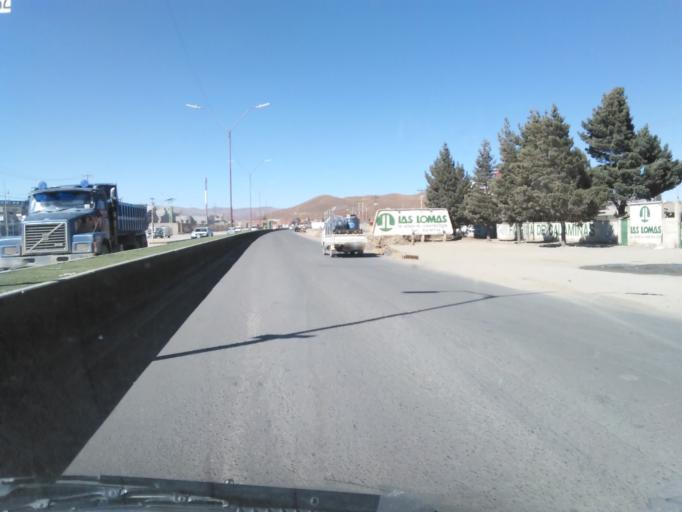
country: BO
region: Oruro
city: Oruro
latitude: -17.9774
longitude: -67.0606
